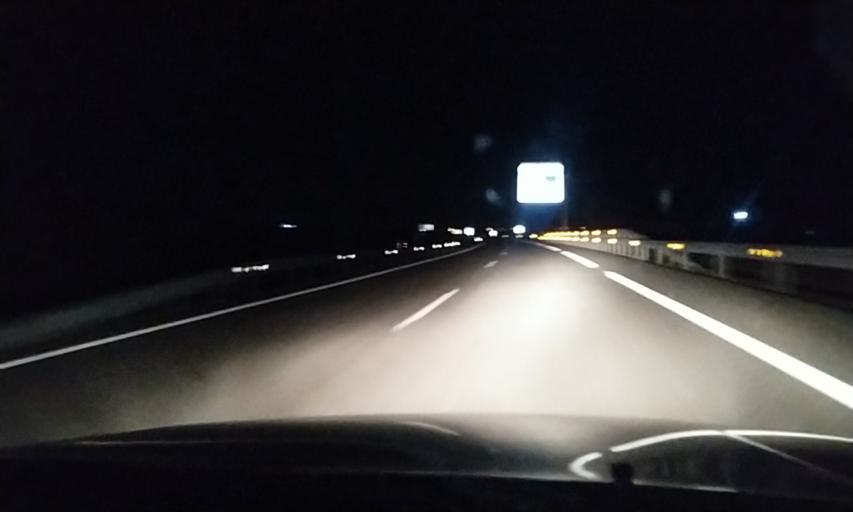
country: ES
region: Castille and Leon
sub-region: Provincia de Leon
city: La Baneza
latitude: 42.2942
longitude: -5.9260
